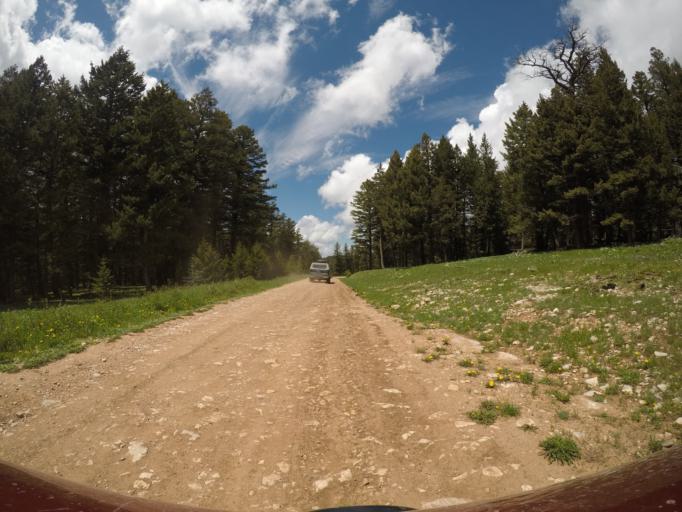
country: US
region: Wyoming
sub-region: Big Horn County
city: Lovell
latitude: 45.1644
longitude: -108.4070
